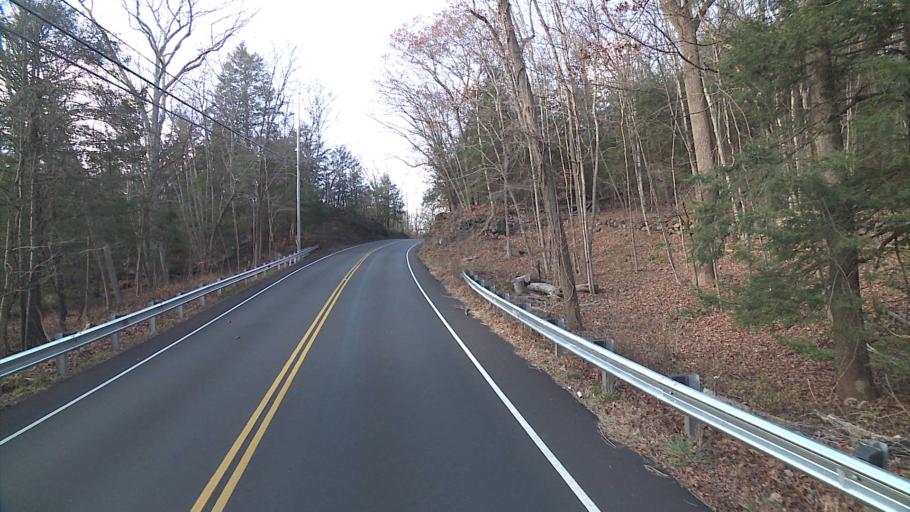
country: US
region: Connecticut
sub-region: Fairfield County
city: Georgetown
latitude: 41.3084
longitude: -73.4097
